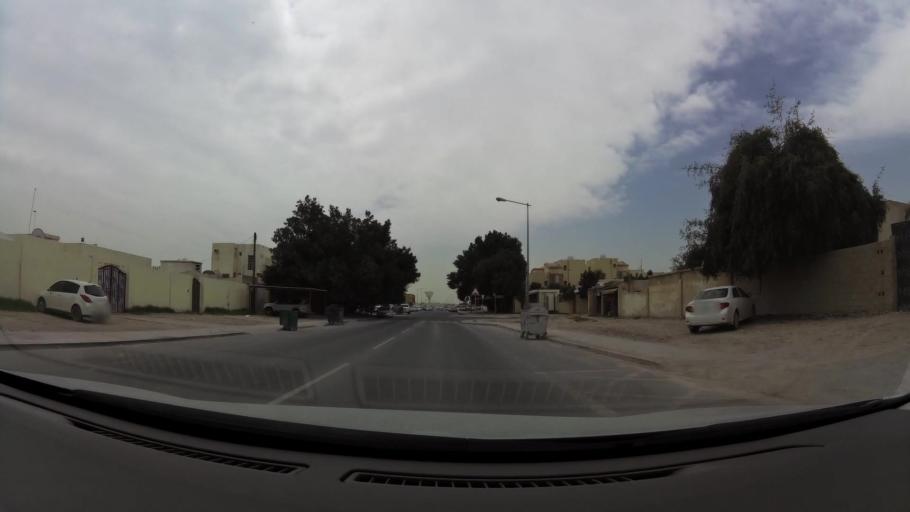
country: QA
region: Baladiyat ar Rayyan
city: Ar Rayyan
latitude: 25.2921
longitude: 51.4589
